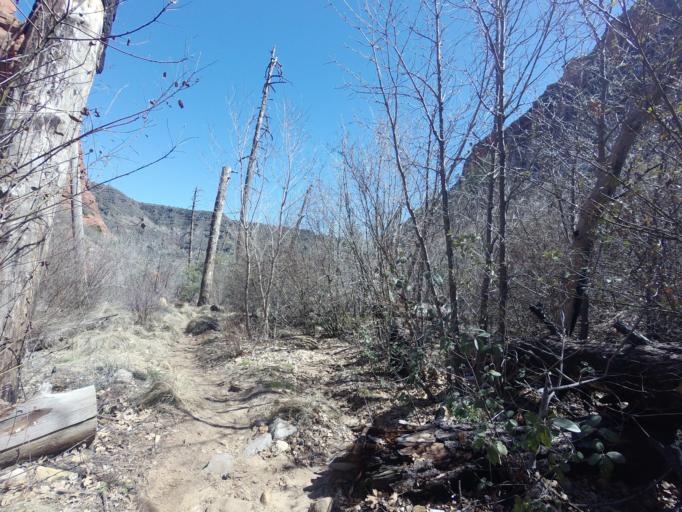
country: US
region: Arizona
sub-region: Coconino County
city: Sedona
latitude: 34.9345
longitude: -111.7536
